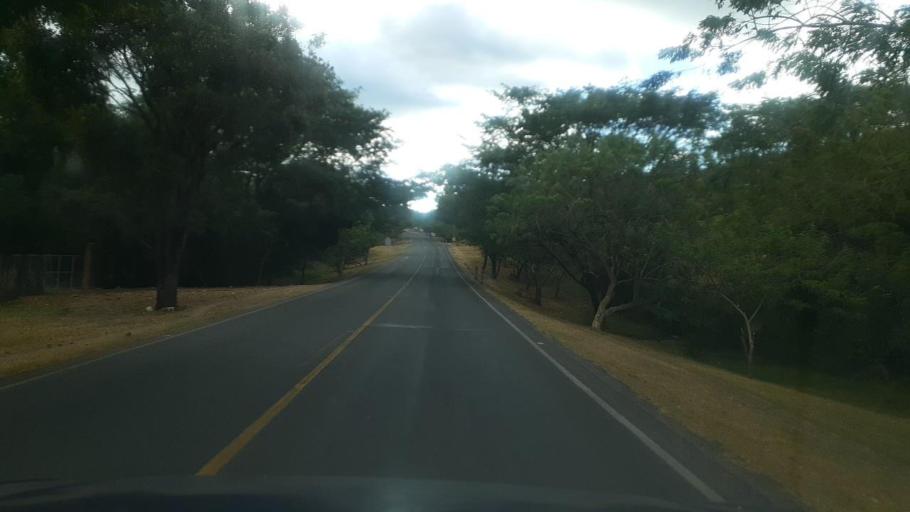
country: NI
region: Madriz
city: Somoto
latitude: 13.4761
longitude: -86.5955
